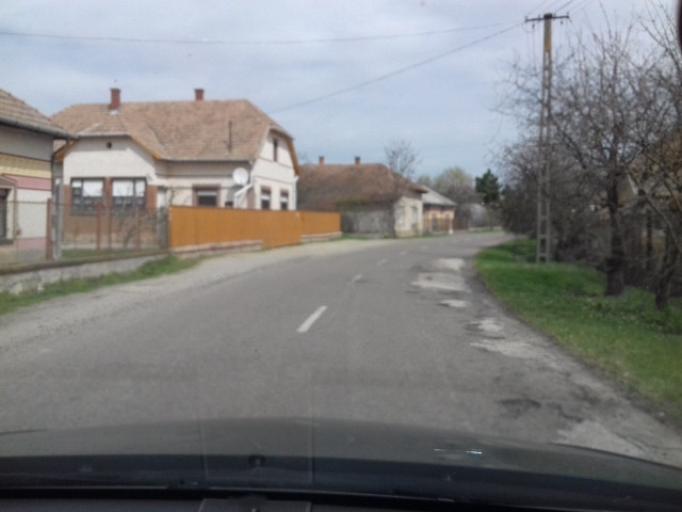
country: HU
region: Bacs-Kiskun
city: Tiszakecske
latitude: 46.9045
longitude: 20.1465
